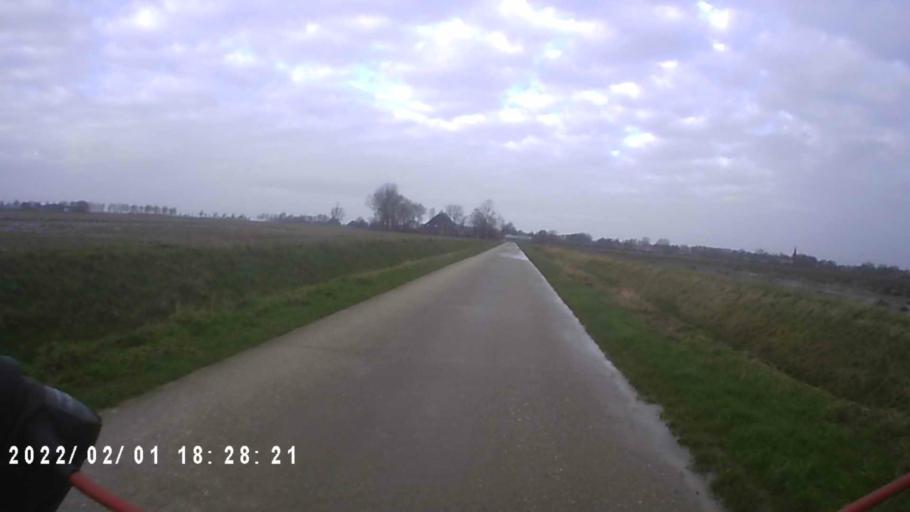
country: NL
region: Groningen
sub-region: Gemeente De Marne
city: Ulrum
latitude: 53.3514
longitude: 6.3193
